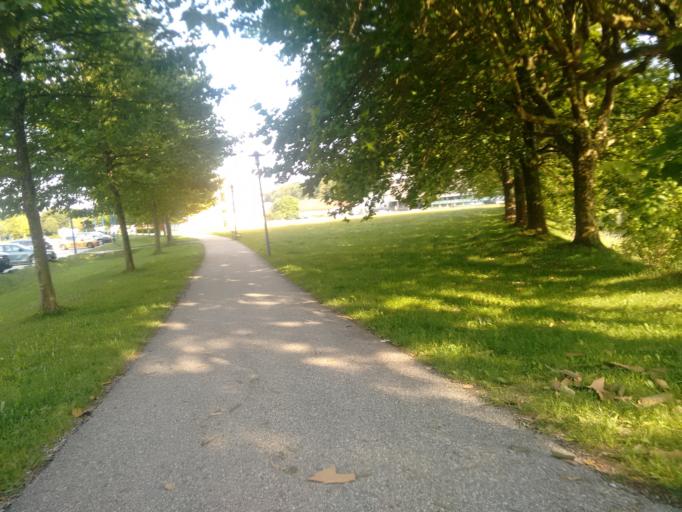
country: AT
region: Upper Austria
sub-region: Politischer Bezirk Grieskirchen
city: Bad Schallerbach
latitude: 48.2282
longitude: 13.9194
